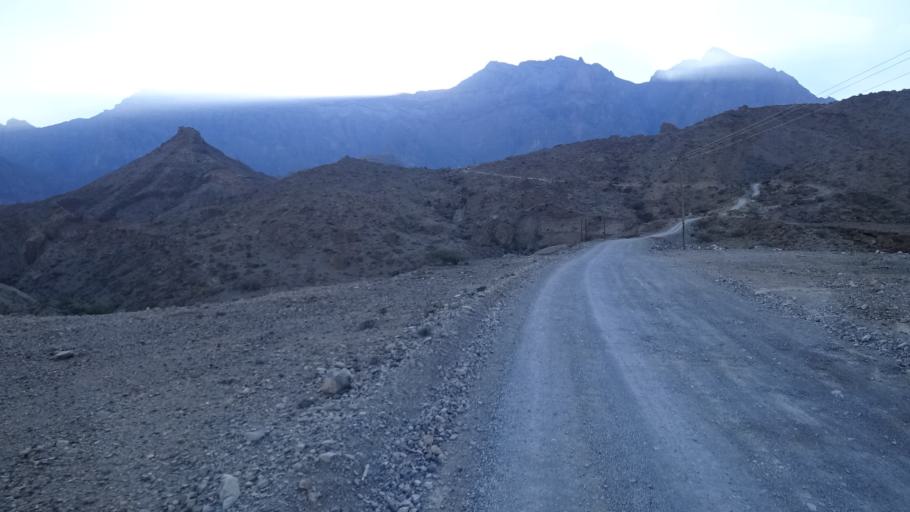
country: OM
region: Al Batinah
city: Rustaq
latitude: 23.2633
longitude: 57.3198
